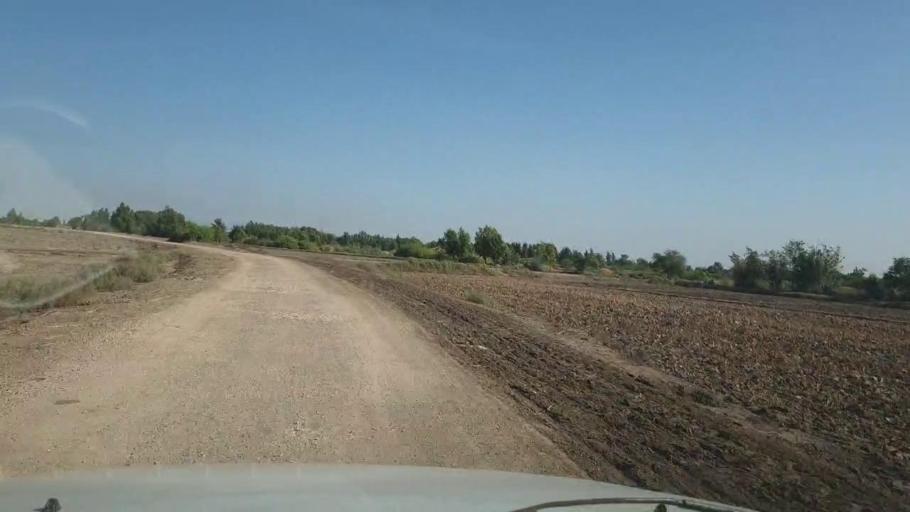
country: PK
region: Sindh
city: Mirpur Sakro
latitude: 24.4843
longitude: 67.8162
